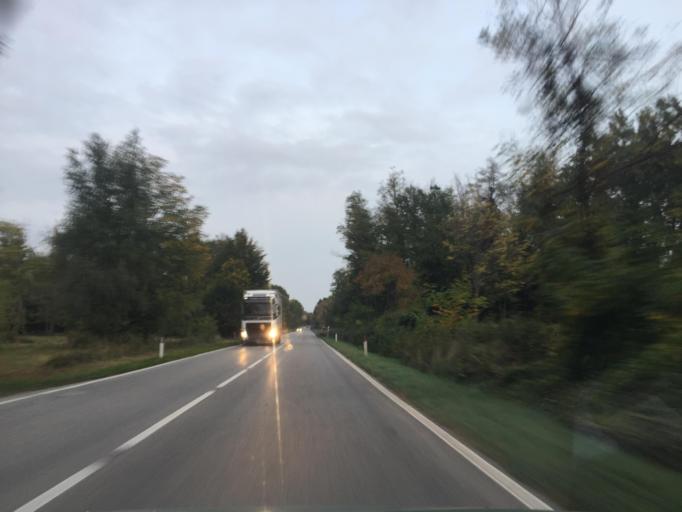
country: IT
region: Friuli Venezia Giulia
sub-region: Provincia di Pordenone
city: Fanna
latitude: 46.1702
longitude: 12.7529
